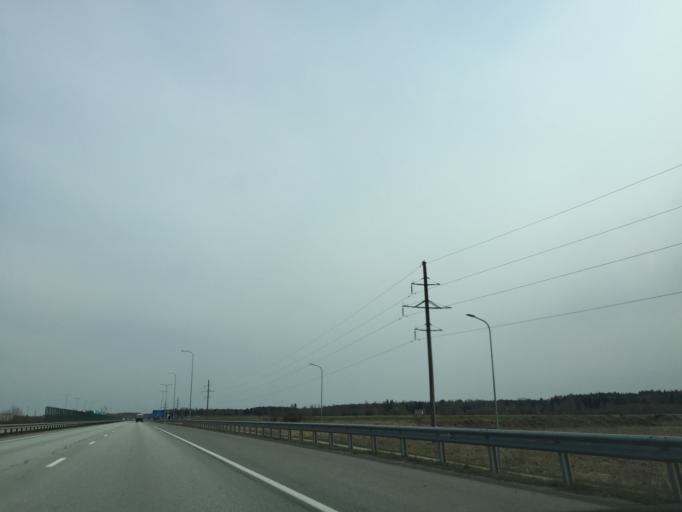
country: LV
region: Marupe
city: Marupe
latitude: 56.8251
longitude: 24.0261
